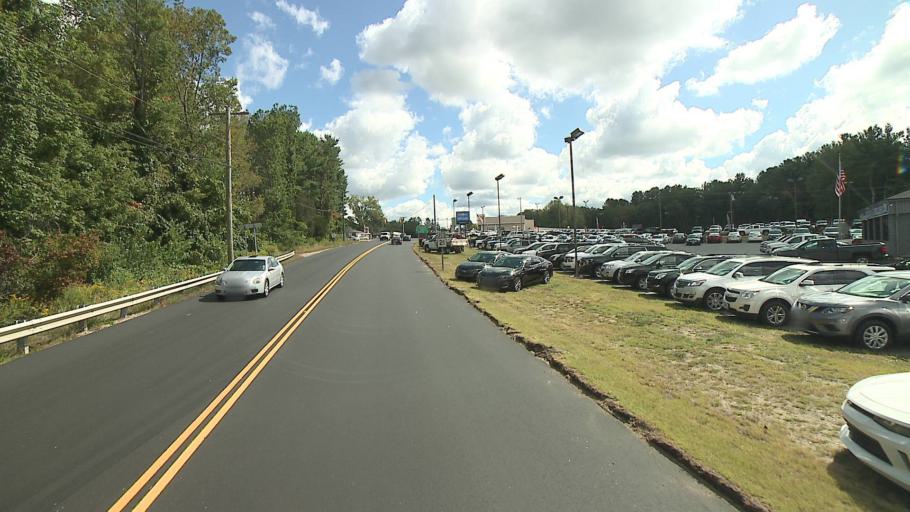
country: US
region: Connecticut
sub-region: Windham County
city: Thompson
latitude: 41.9265
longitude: -71.8699
